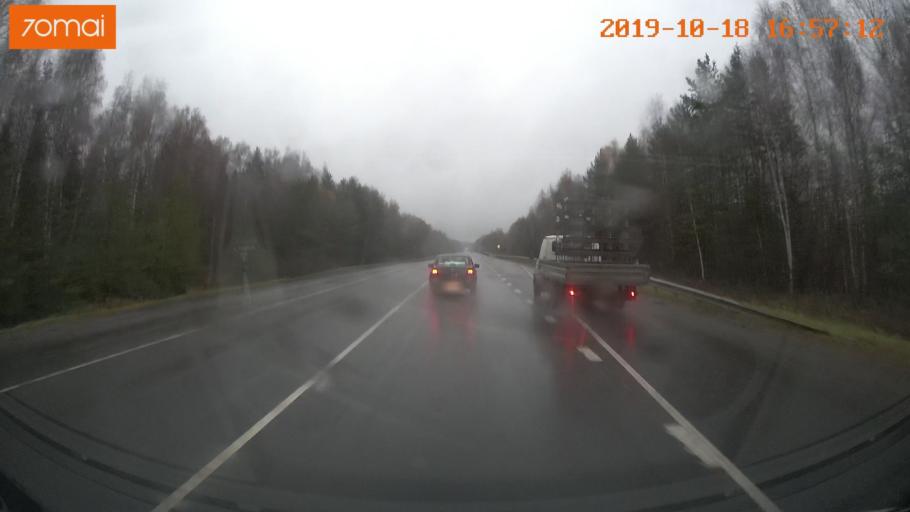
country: RU
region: Ivanovo
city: Novoye Leushino
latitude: 56.6646
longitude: 40.5932
